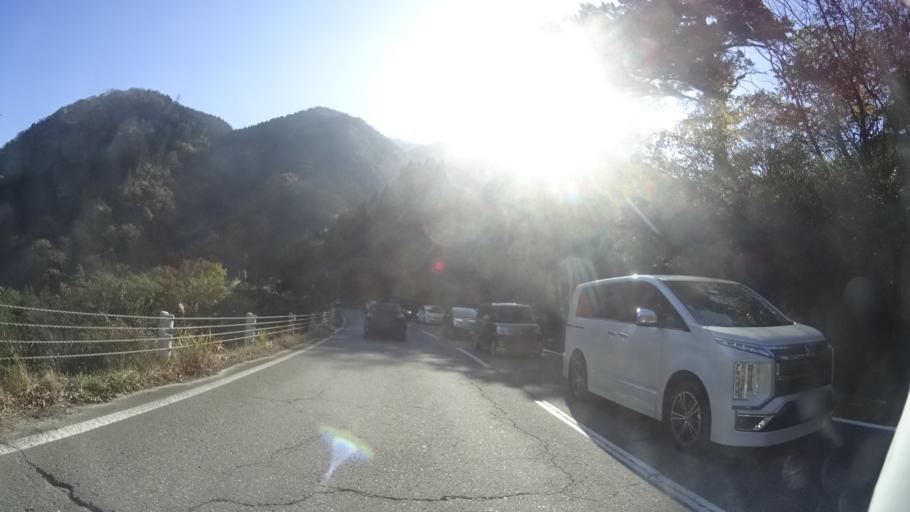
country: JP
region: Fukui
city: Ono
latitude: 35.9637
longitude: 136.6057
